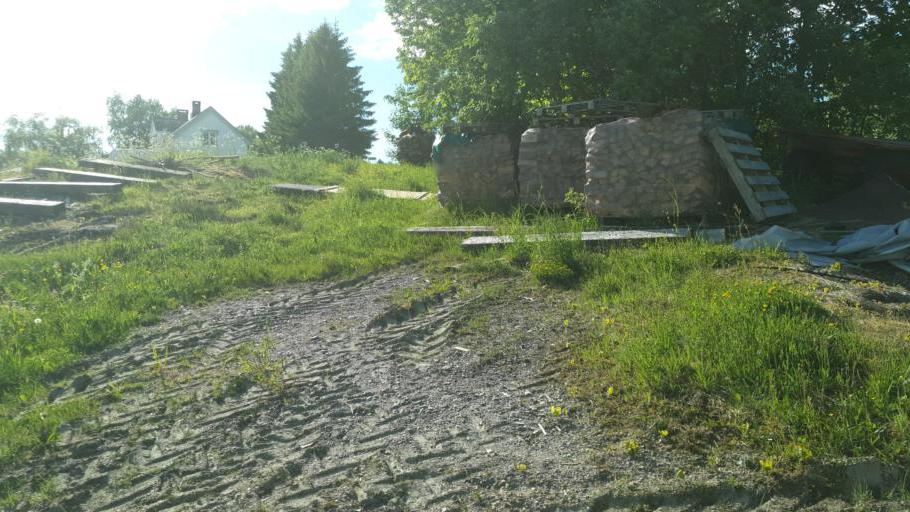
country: NO
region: Sor-Trondelag
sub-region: Rissa
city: Rissa
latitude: 63.4971
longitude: 10.0909
